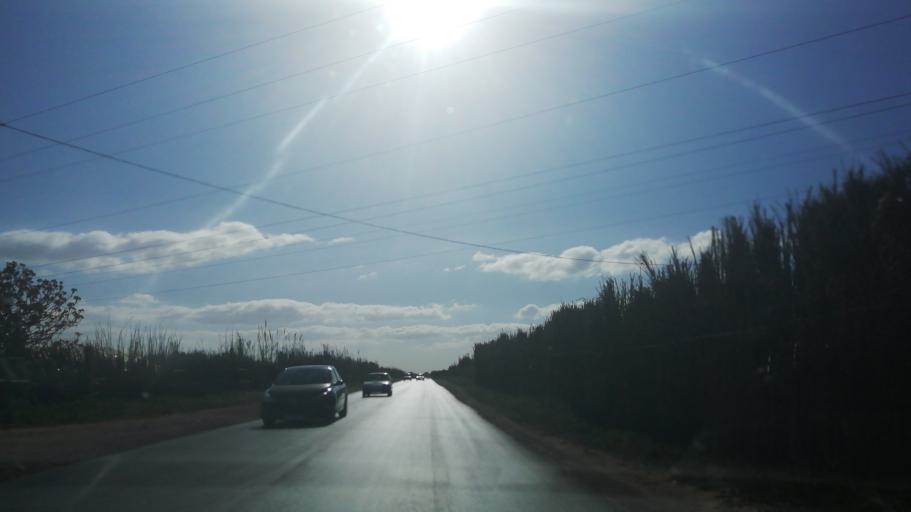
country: DZ
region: Mostaganem
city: Mostaganem
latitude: 35.9716
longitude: 0.2673
